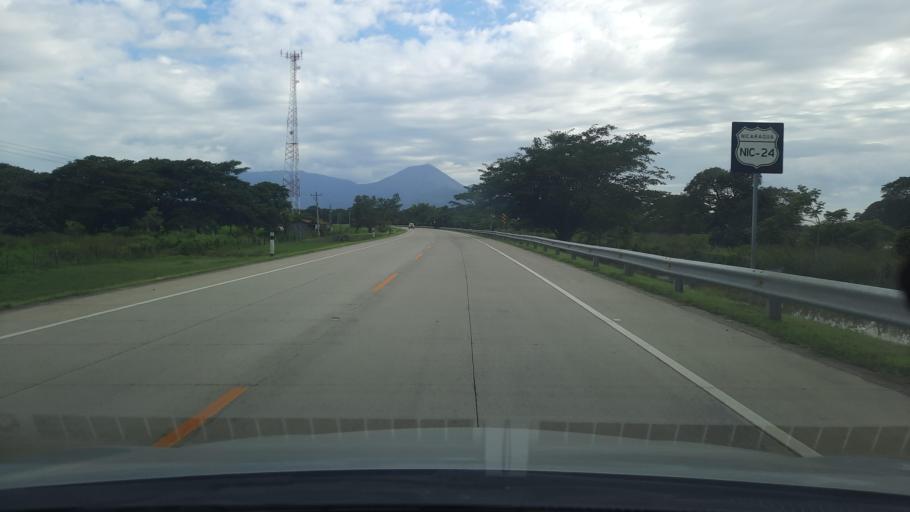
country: NI
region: Chinandega
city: Somotillo
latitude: 12.8345
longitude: -86.8932
